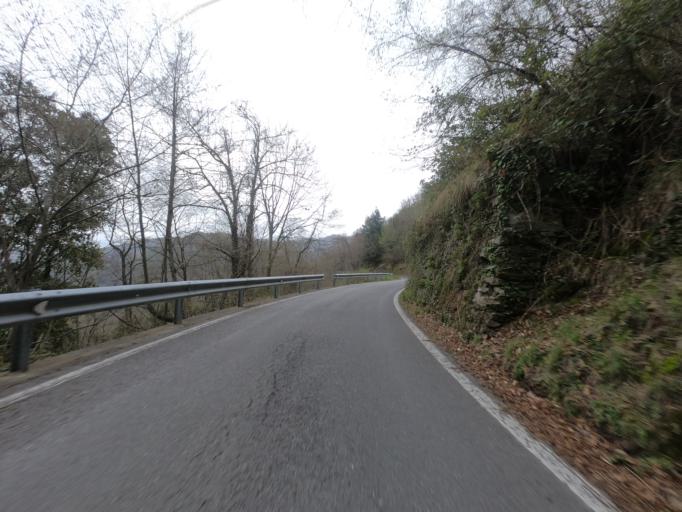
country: IT
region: Liguria
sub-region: Provincia di Savona
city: Testico
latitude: 44.0306
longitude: 8.0149
